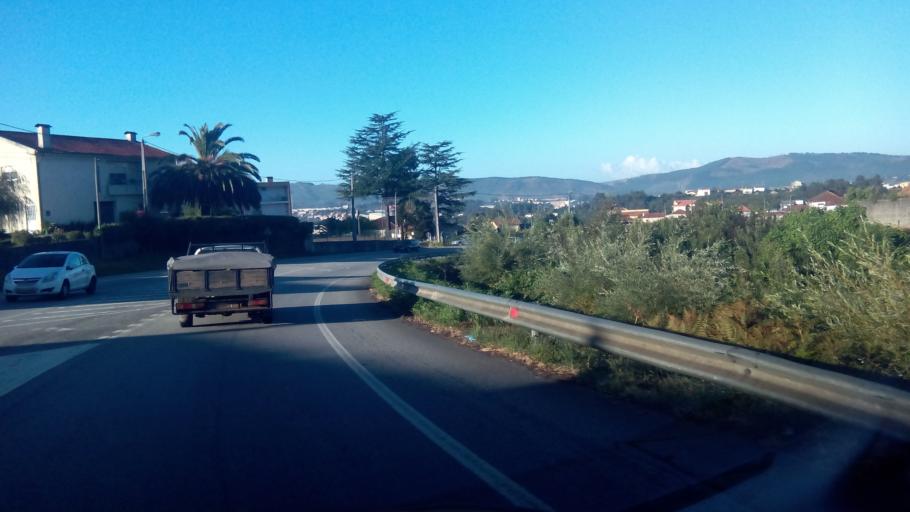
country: PT
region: Porto
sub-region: Paredes
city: Gandra
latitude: 41.1959
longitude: -8.4256
